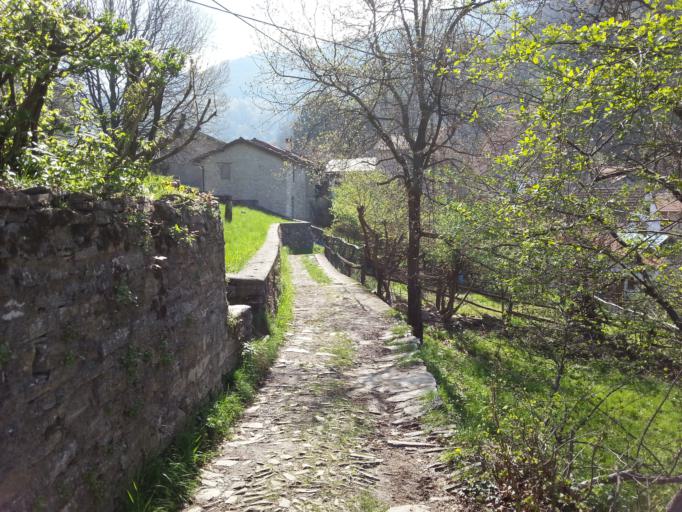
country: IT
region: Lombardy
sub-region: Provincia di Como
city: Torno
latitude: 45.8497
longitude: 9.1217
